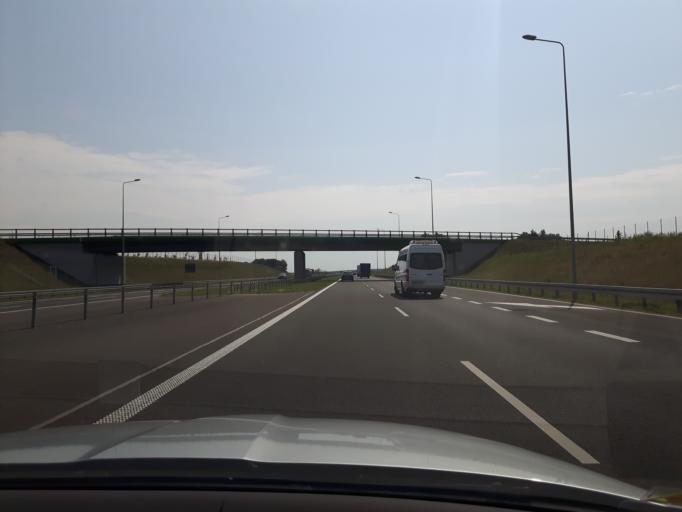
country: PL
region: Warmian-Masurian Voivodeship
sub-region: Powiat nidzicki
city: Nidzica
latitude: 53.2963
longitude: 20.4369
